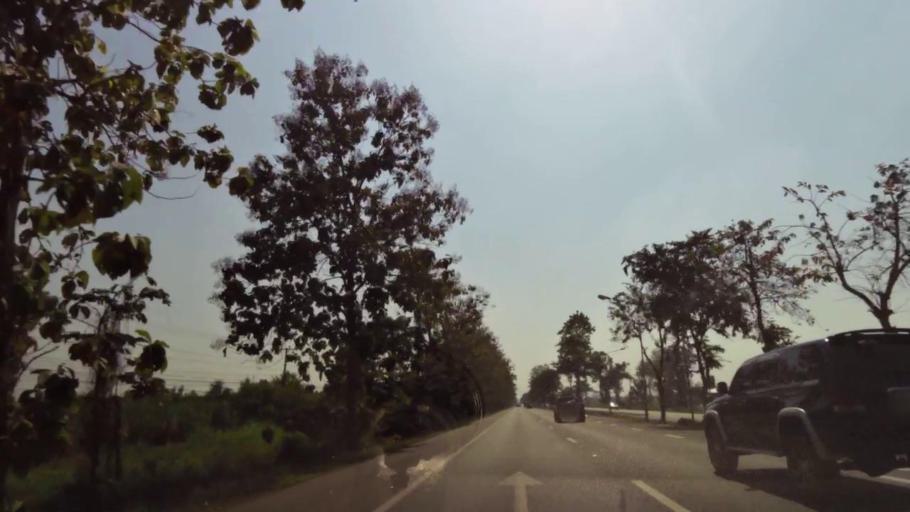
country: TH
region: Phichit
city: Bueng Na Rang
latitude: 16.0897
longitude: 100.1251
